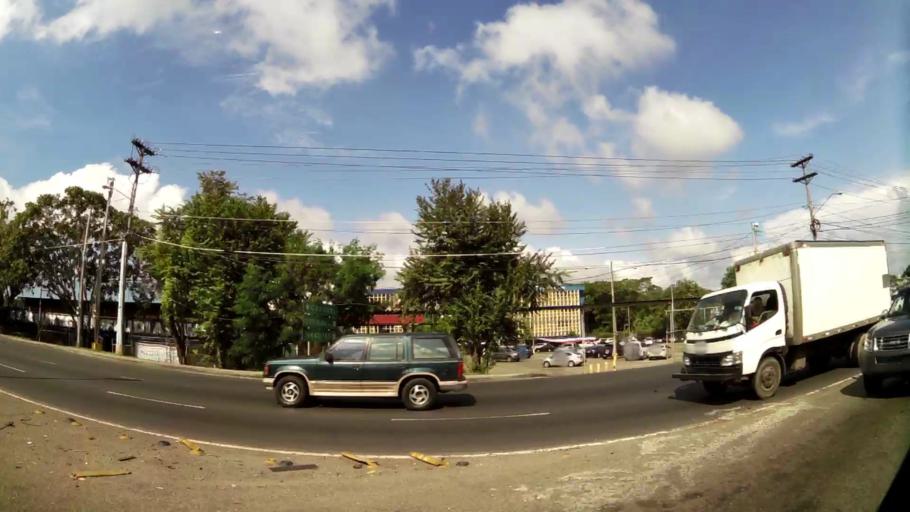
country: PA
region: Panama
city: Panama
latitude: 8.9821
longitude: -79.5364
